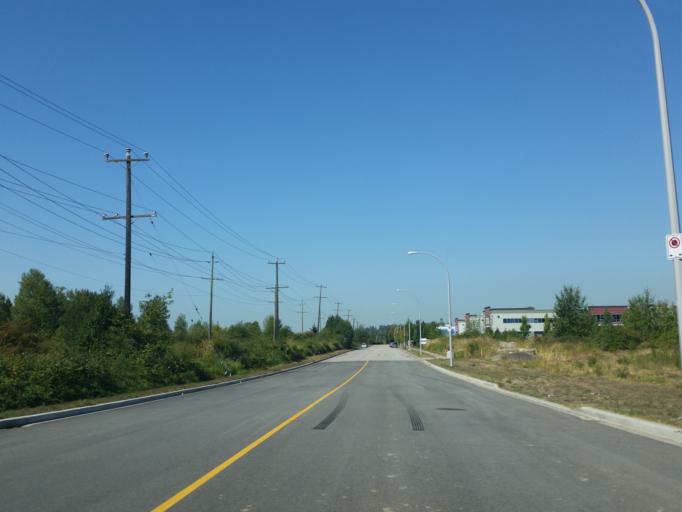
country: CA
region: British Columbia
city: Langley
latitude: 49.0971
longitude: -122.7022
